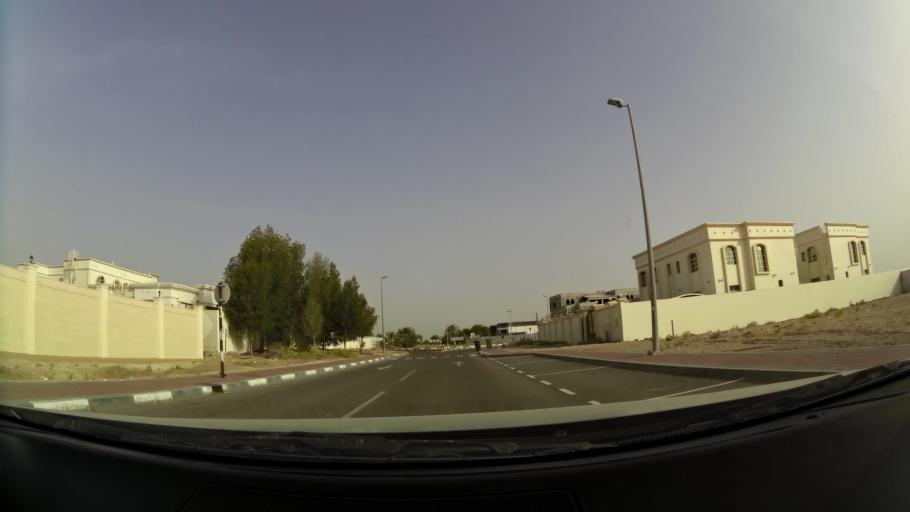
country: AE
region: Abu Dhabi
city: Al Ain
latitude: 24.1283
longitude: 55.6984
